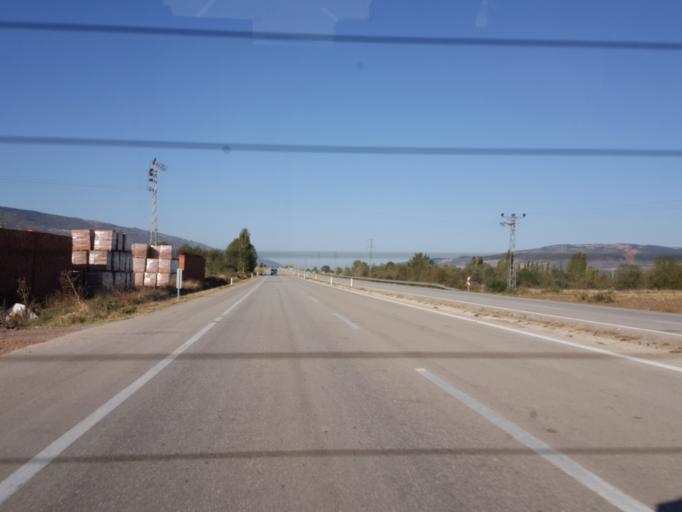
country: TR
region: Amasya
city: Ezinepazari
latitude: 40.5698
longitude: 36.0881
